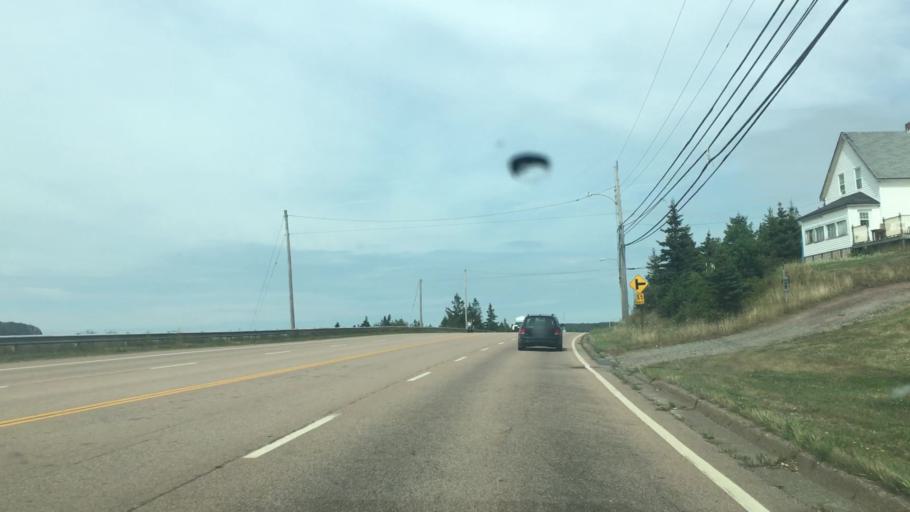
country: CA
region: Nova Scotia
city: Port Hawkesbury
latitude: 45.6272
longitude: -61.3728
